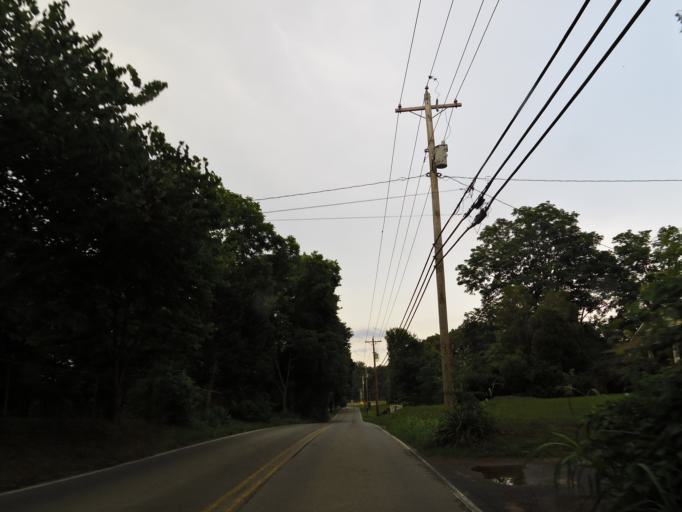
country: US
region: Tennessee
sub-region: Blount County
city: Wildwood
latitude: 35.8008
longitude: -83.8642
